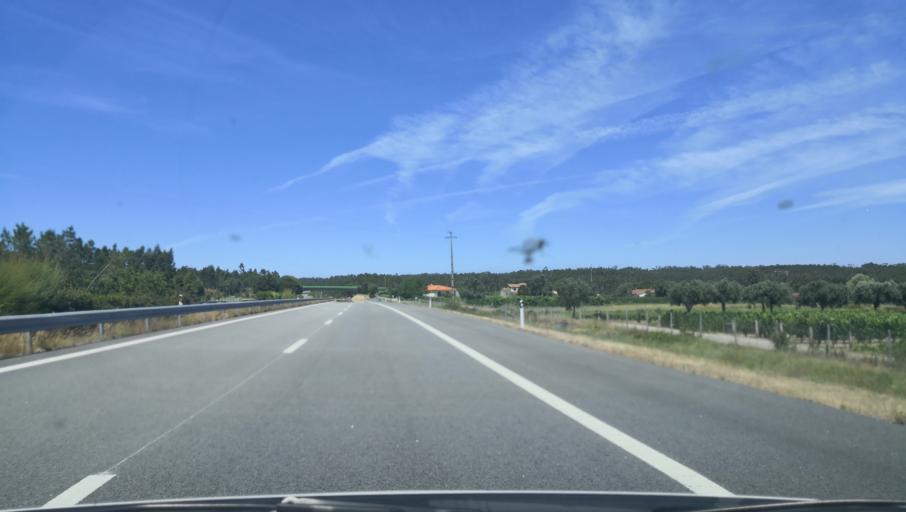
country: PT
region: Coimbra
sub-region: Montemor-O-Velho
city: Arazede
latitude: 40.2340
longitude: -8.6642
